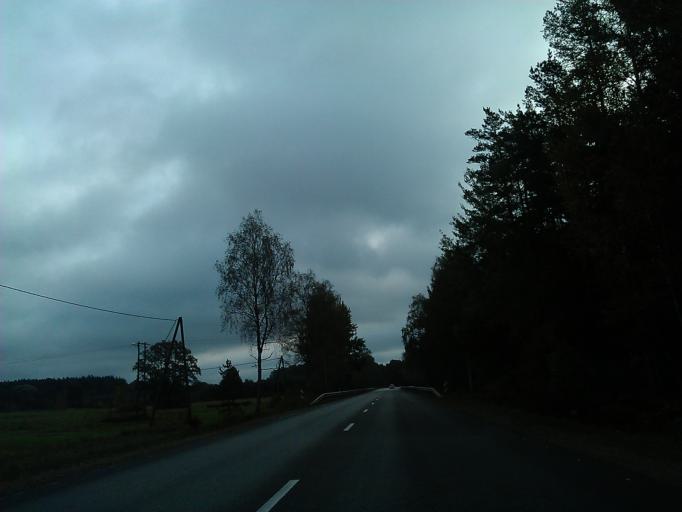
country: LV
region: Ikskile
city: Ikskile
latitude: 56.8923
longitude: 24.4617
